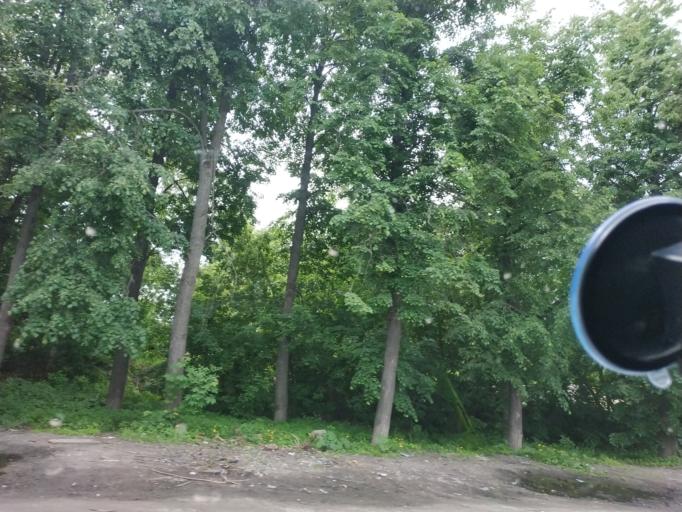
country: RU
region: Moskovskaya
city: Zhukovskiy
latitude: 55.5550
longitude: 38.1188
